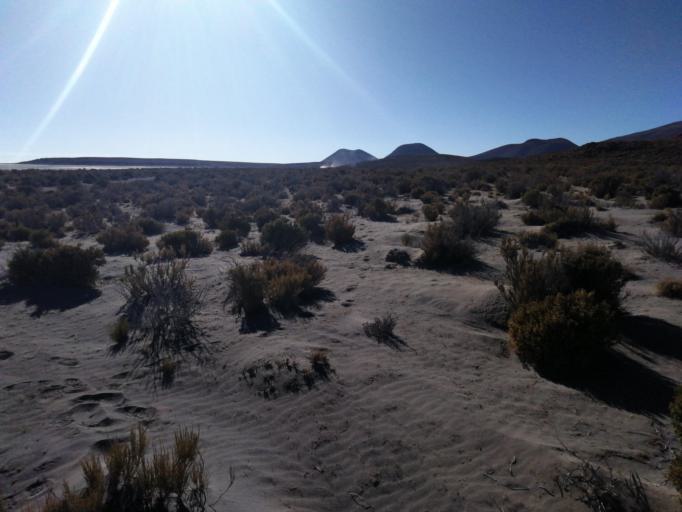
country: BO
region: Oruro
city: Cruz de Machacamarca
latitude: -19.2568
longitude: -68.3233
